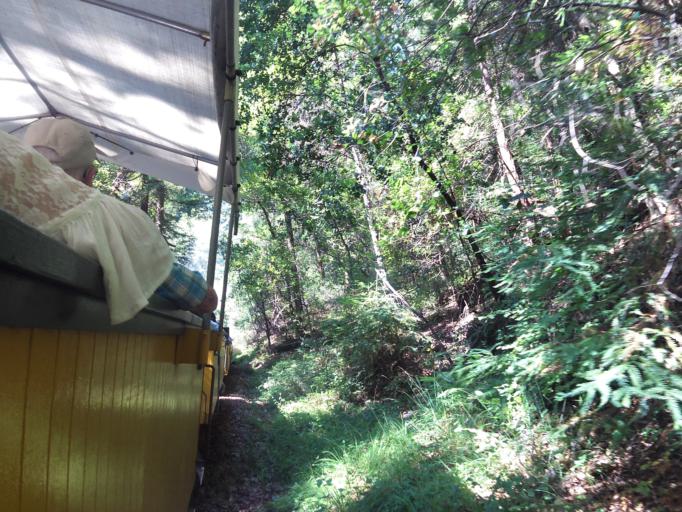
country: US
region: California
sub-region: Santa Cruz County
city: Mount Hermon
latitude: 37.0418
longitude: -122.0585
